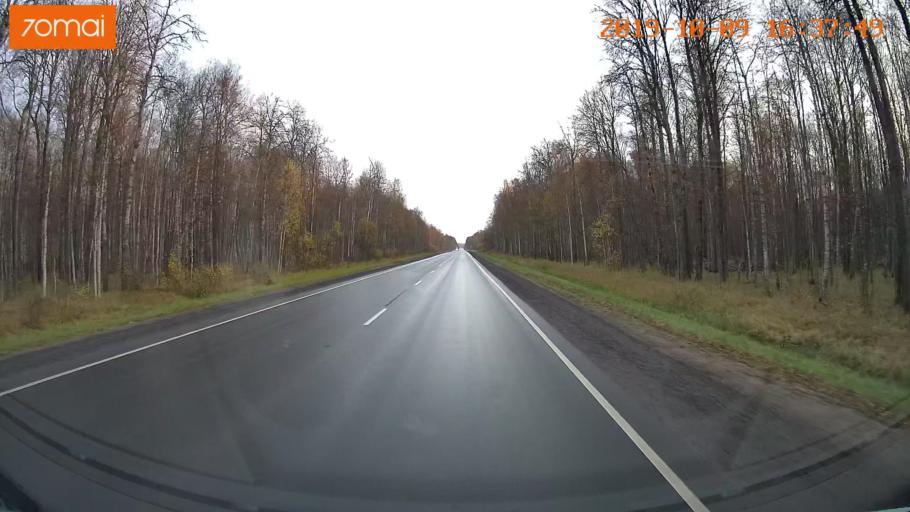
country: RU
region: Kostroma
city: Volgorechensk
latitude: 57.5211
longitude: 41.0294
